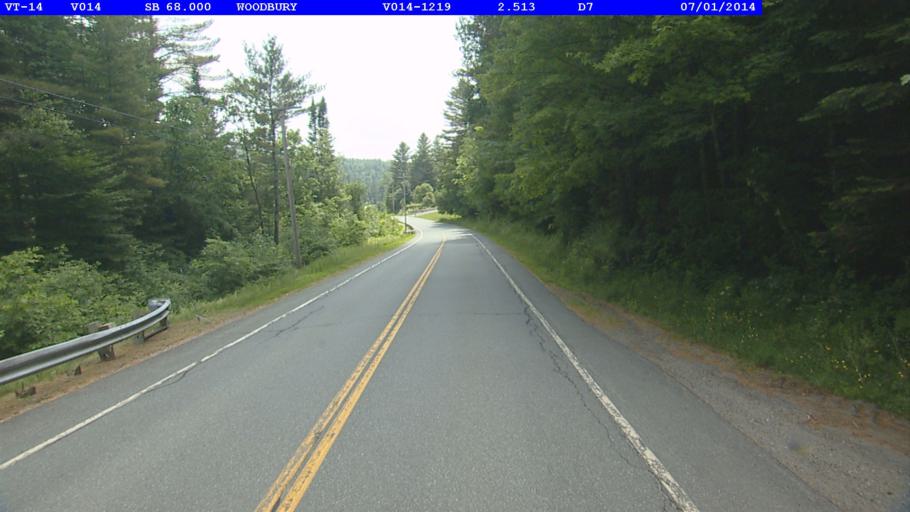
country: US
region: Vermont
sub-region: Caledonia County
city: Hardwick
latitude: 44.4245
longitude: -72.4121
